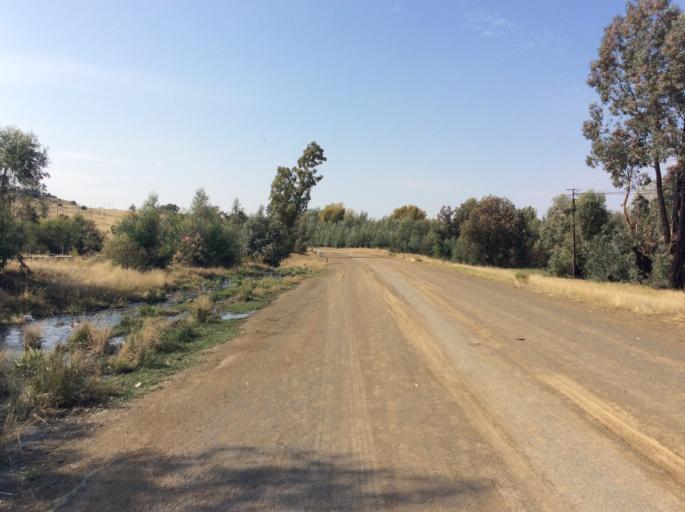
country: LS
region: Mafeteng
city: Mafeteng
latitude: -29.7245
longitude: 27.0246
